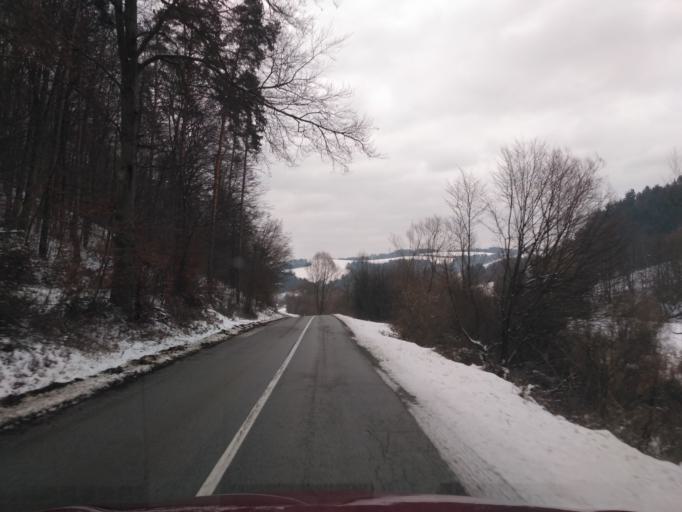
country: SK
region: Presovsky
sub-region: Okres Presov
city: Presov
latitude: 48.9616
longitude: 21.1037
